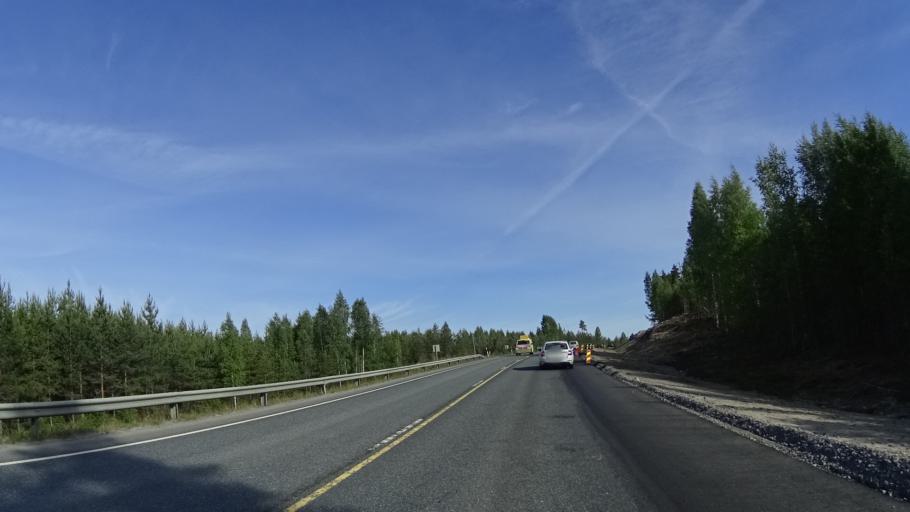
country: FI
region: Haeme
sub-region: Forssa
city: Tammela
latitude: 60.7382
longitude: 23.7429
